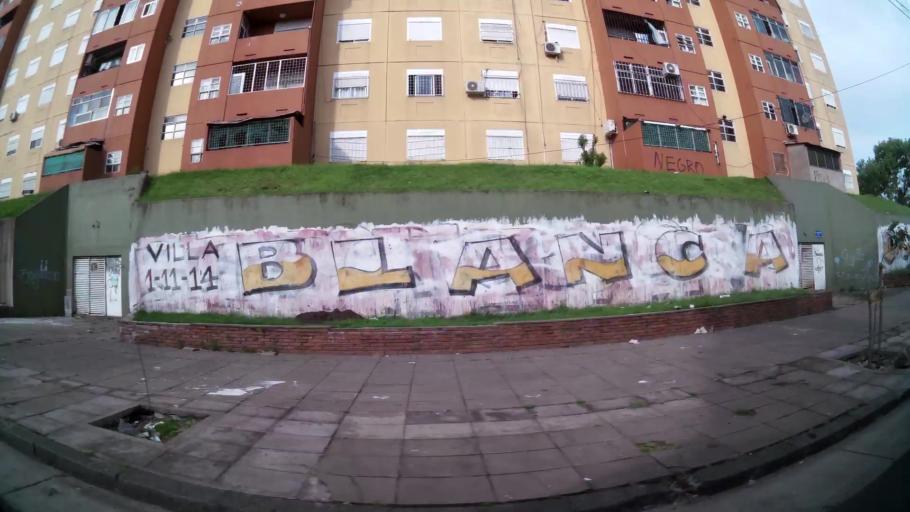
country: AR
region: Buenos Aires F.D.
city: Villa Lugano
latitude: -34.6482
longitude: -58.4568
